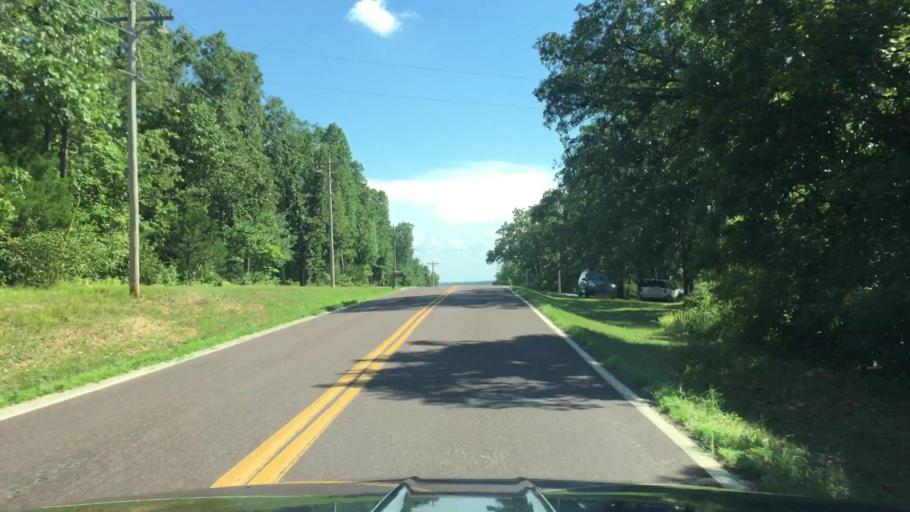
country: US
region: Missouri
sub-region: Miller County
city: Tuscumbia
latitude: 38.1150
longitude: -92.4719
